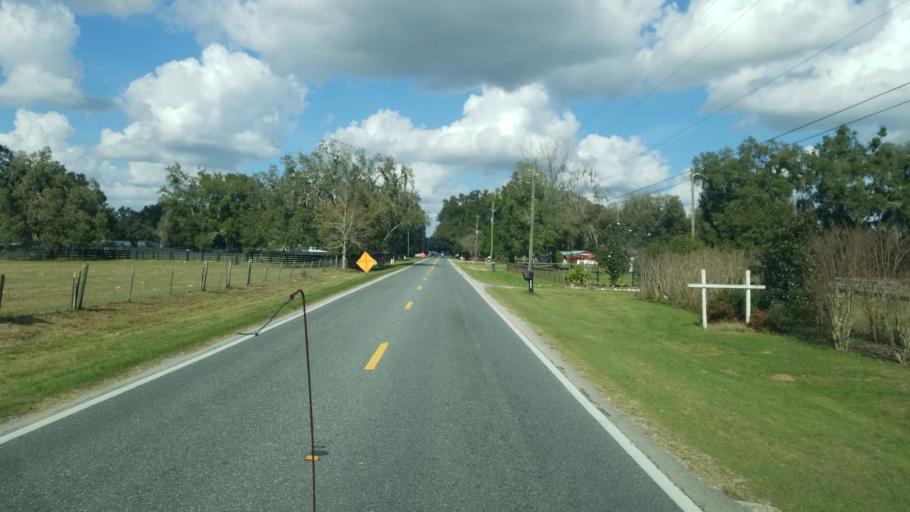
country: US
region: Florida
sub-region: Marion County
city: Belleview
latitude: 29.0065
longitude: -82.1199
